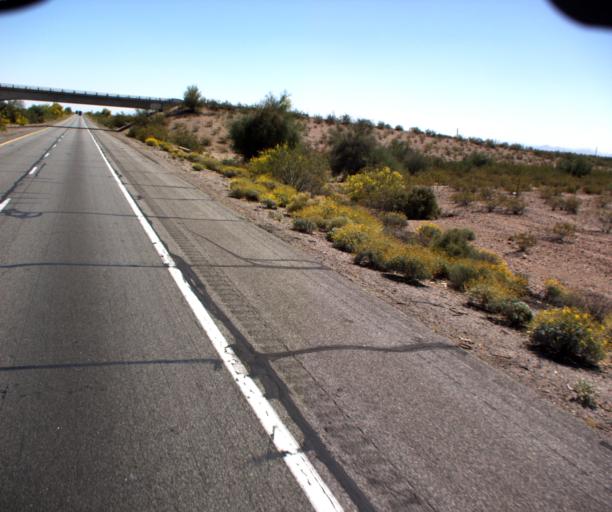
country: US
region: Arizona
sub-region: Maricopa County
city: Buckeye
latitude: 33.4705
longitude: -112.8172
